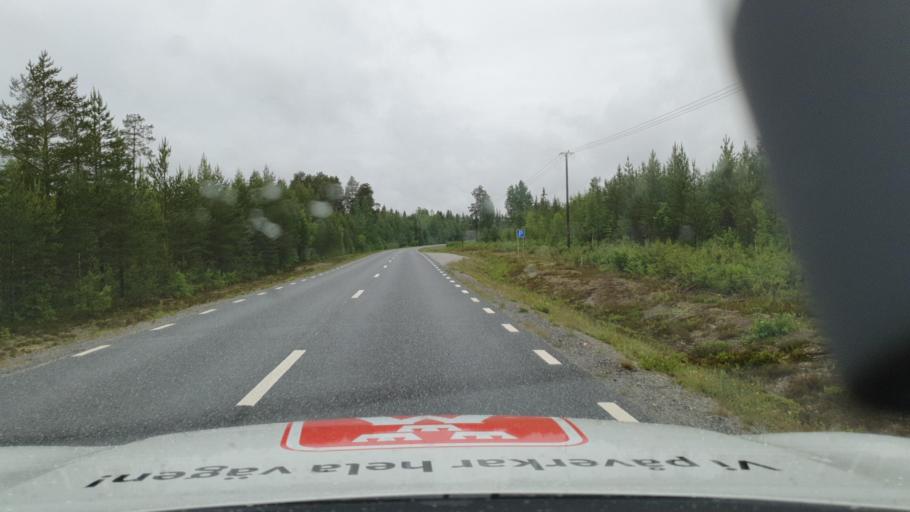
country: SE
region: Vaesterbotten
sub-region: Asele Kommun
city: Asele
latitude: 63.9679
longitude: 17.2646
